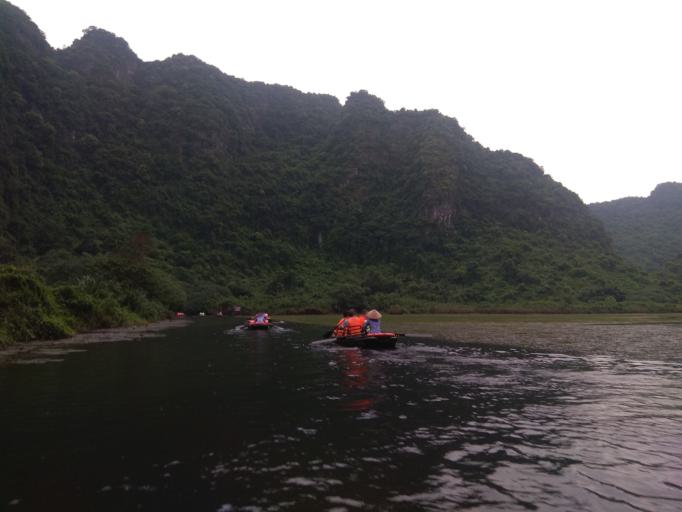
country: VN
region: Ninh Binh
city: Thi Tran Thien Ton
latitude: 20.2612
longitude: 105.8989
